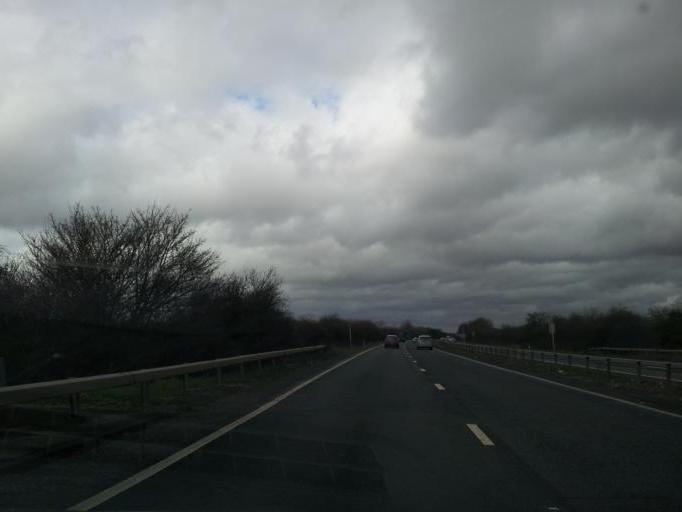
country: GB
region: England
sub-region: Somerset
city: Ilchester
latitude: 51.0034
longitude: -2.6920
